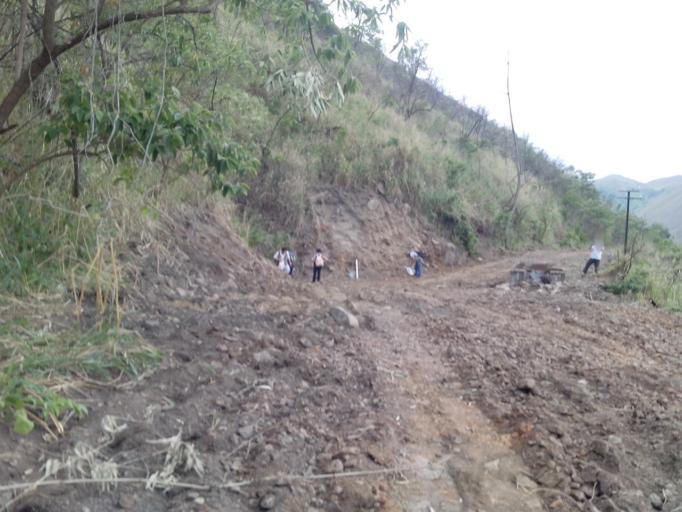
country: BR
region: Rio de Janeiro
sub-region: Miguel Pereira
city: Miguel Pereira
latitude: -22.4991
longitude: -43.4979
